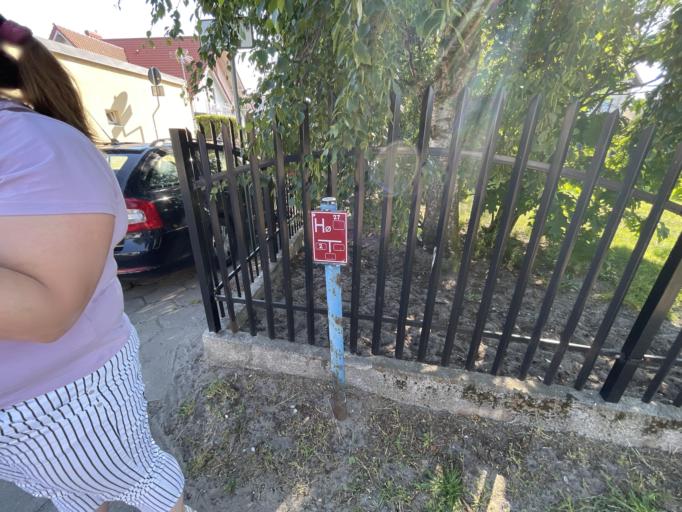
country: PL
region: Pomeranian Voivodeship
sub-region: Powiat pucki
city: Jastarnia
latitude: 54.6966
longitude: 18.6850
